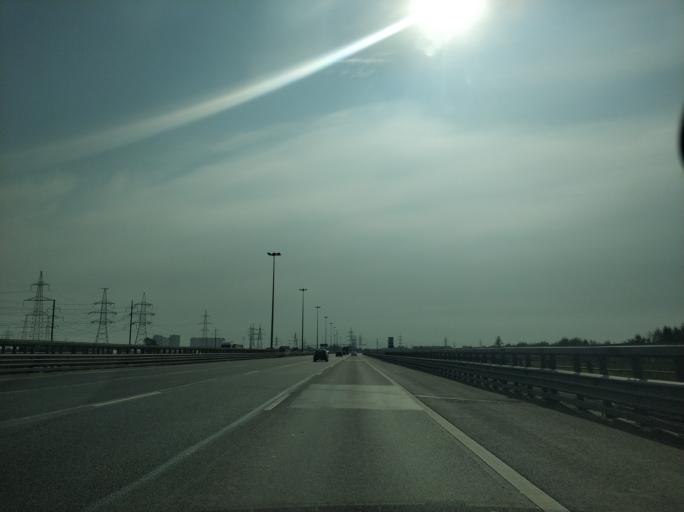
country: RU
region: Leningrad
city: Murino
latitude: 60.0253
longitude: 30.4498
